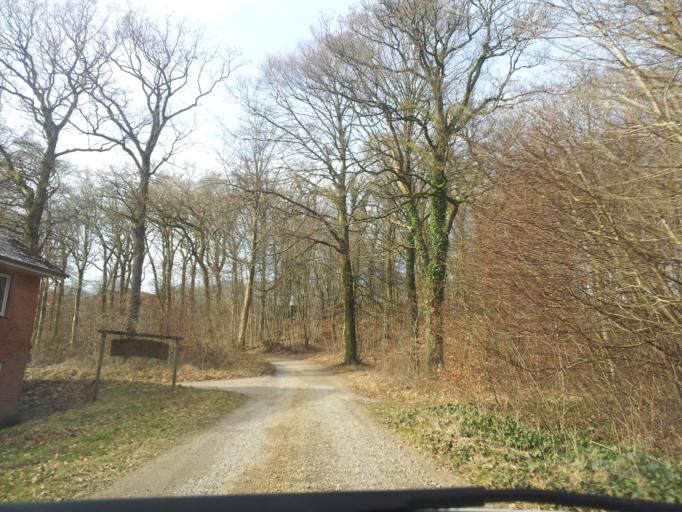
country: DK
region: South Denmark
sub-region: Vejen Kommune
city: Vejen
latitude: 55.4466
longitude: 9.1115
